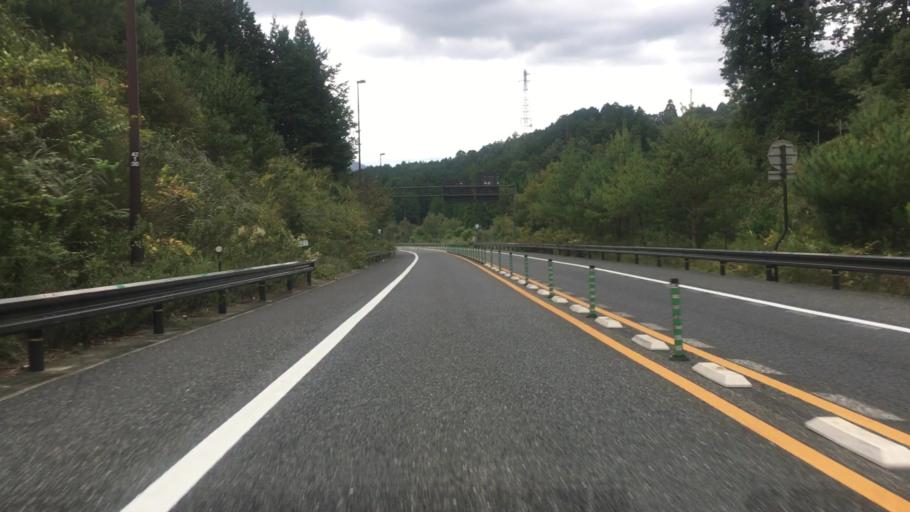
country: JP
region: Kyoto
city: Fukuchiyama
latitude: 35.3036
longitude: 134.9193
